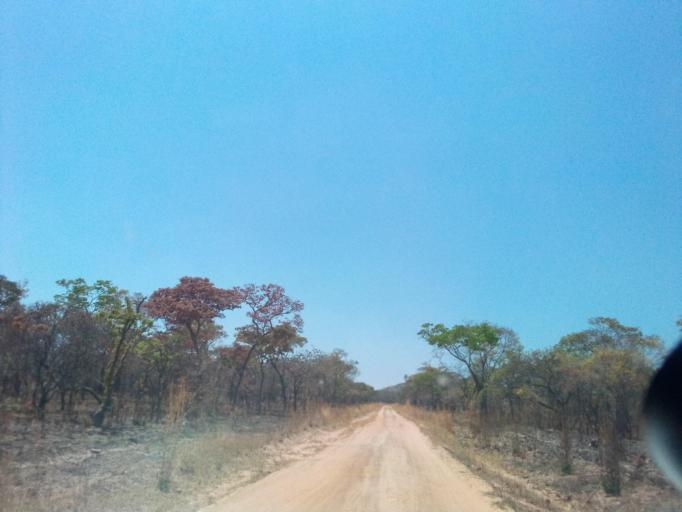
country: ZM
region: Northern
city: Mpika
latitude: -12.2539
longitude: 30.6916
